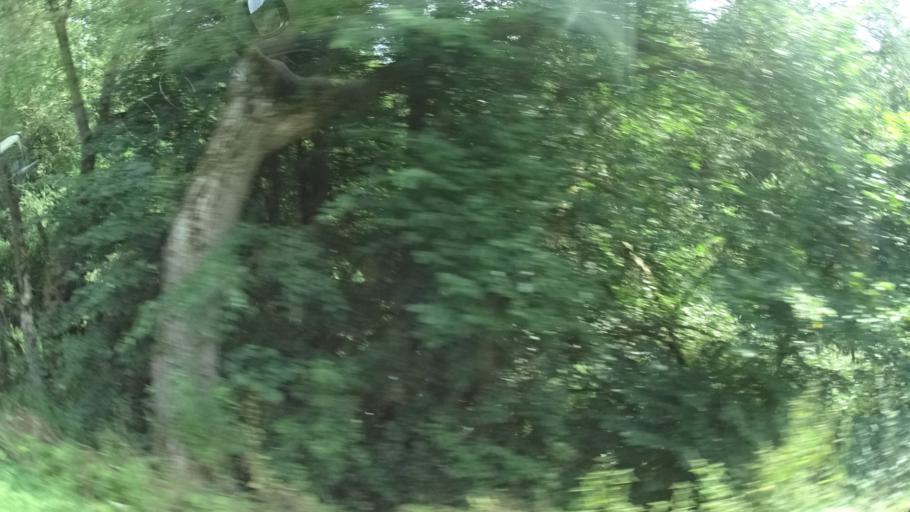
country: DE
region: Hesse
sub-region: Regierungsbezirk Giessen
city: Lauterbach
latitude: 50.6025
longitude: 9.4244
